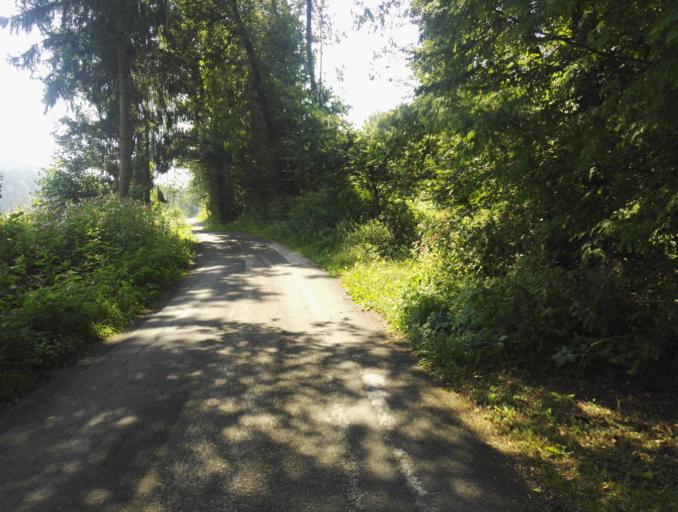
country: AT
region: Styria
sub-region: Politischer Bezirk Graz-Umgebung
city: Eisbach
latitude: 47.1028
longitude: 15.2905
